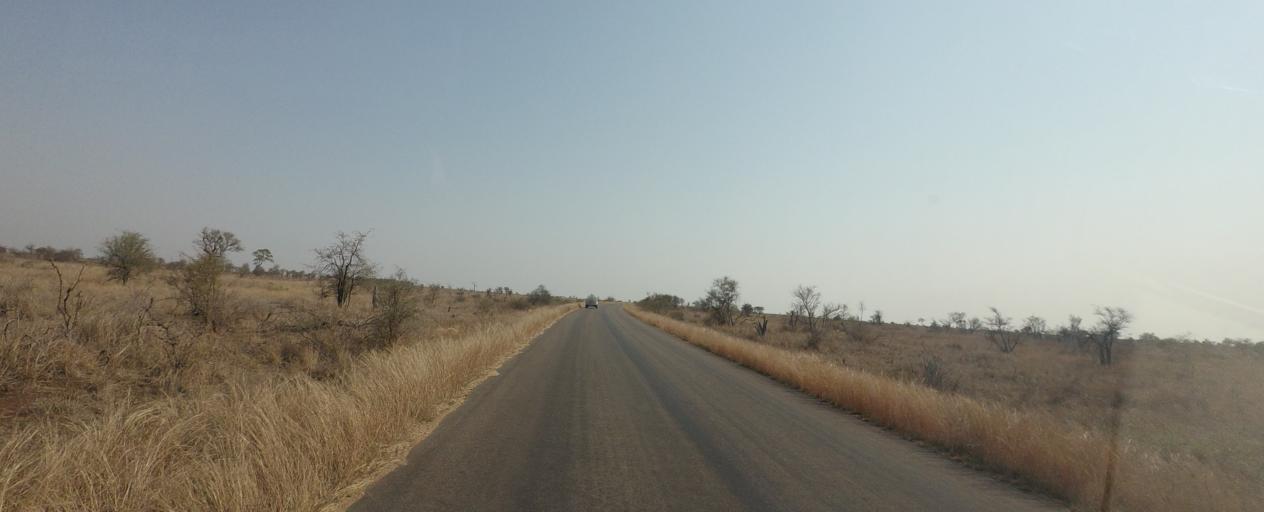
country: ZA
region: Limpopo
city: Thulamahashi
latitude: -24.3622
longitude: 31.7635
